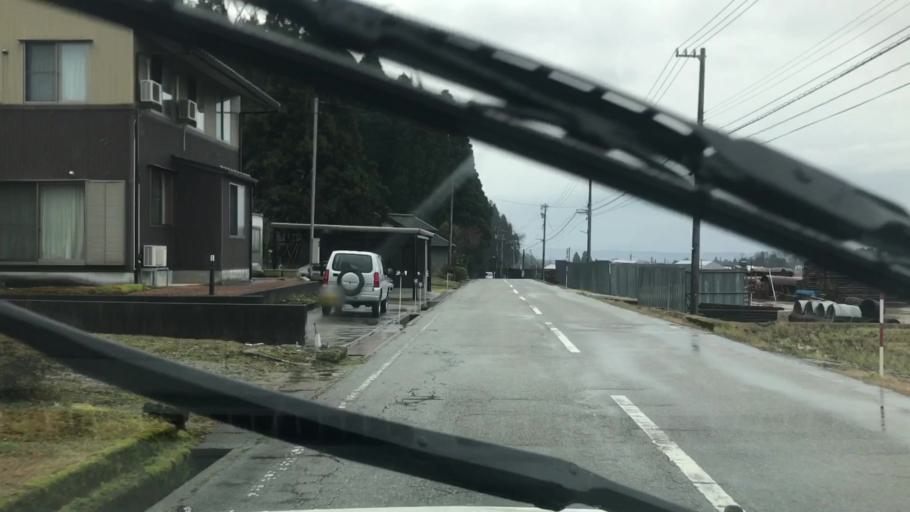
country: JP
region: Toyama
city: Toyama-shi
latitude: 36.6043
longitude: 137.2866
